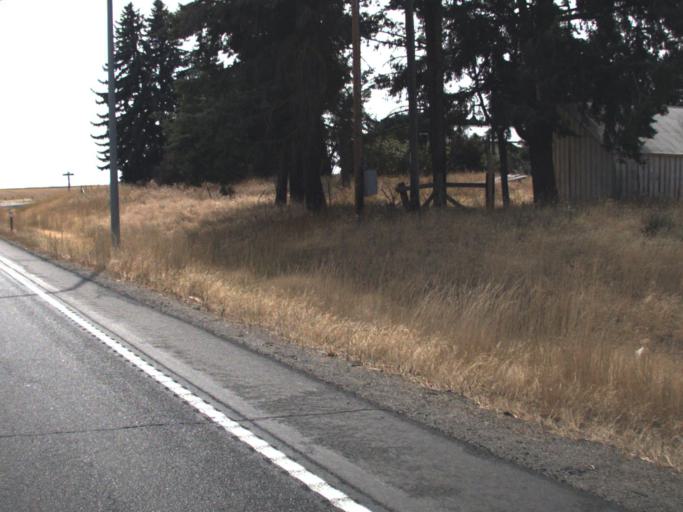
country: US
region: Washington
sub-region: Spokane County
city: Fairwood
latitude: 47.8610
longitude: -117.4219
